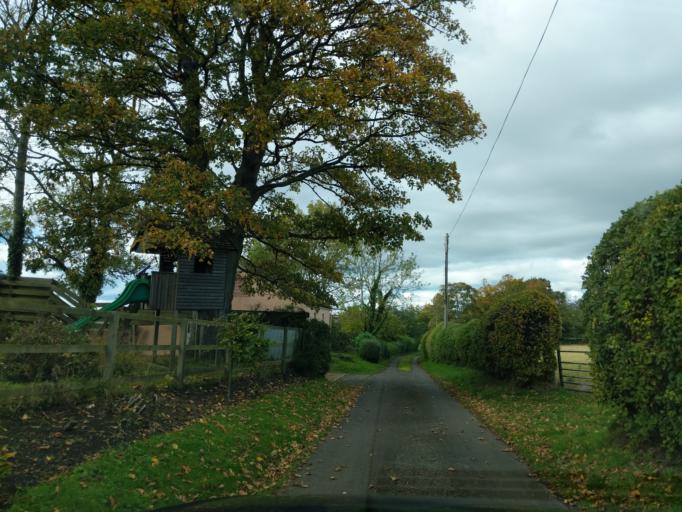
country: GB
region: Scotland
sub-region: East Lothian
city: East Linton
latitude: 55.9421
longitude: -2.7124
